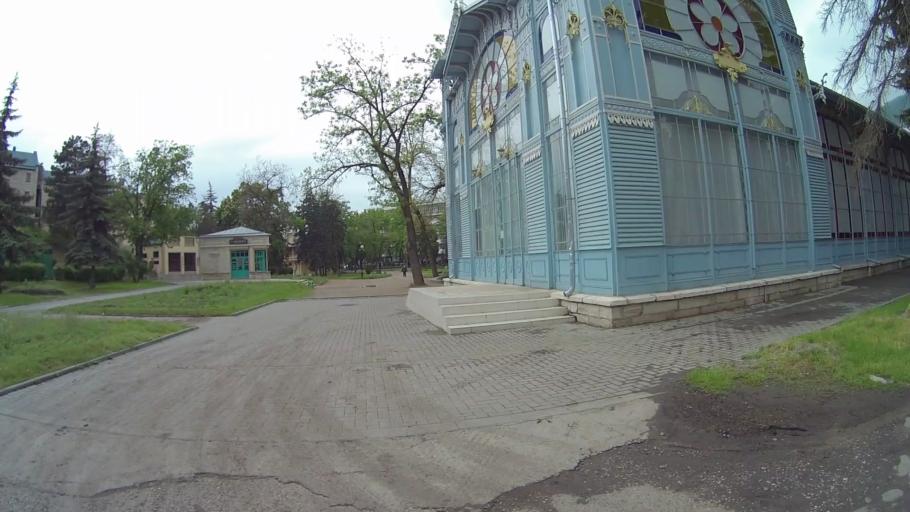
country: RU
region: Stavropol'skiy
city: Goryachevodskiy
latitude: 44.0362
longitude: 43.0817
